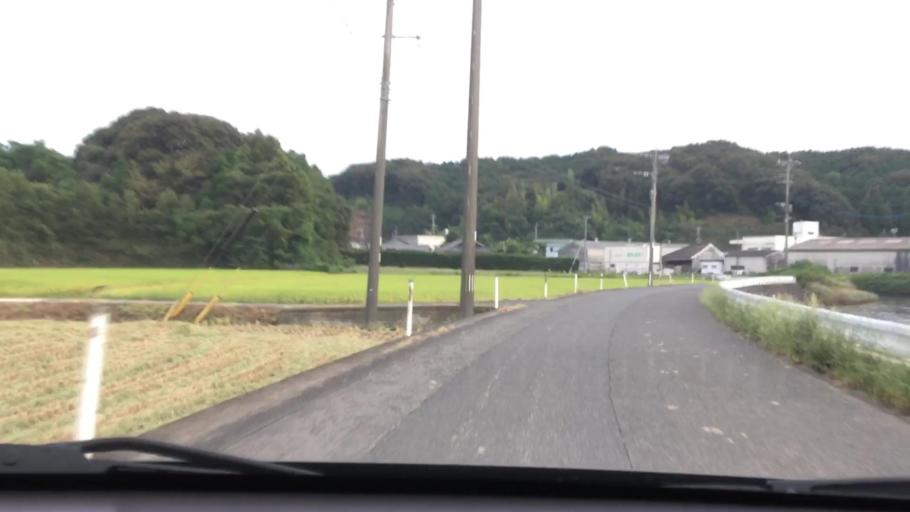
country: JP
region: Nagasaki
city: Togitsu
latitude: 32.9898
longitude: 129.7734
